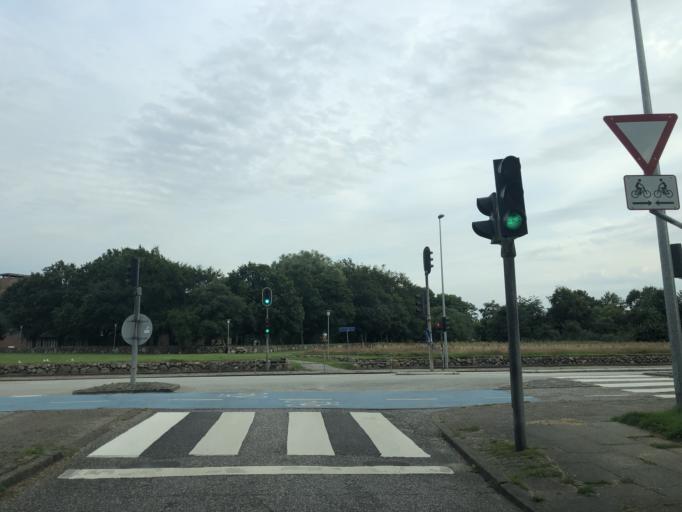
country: DK
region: Central Jutland
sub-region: Herning Kommune
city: Herning
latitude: 56.1455
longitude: 8.9512
